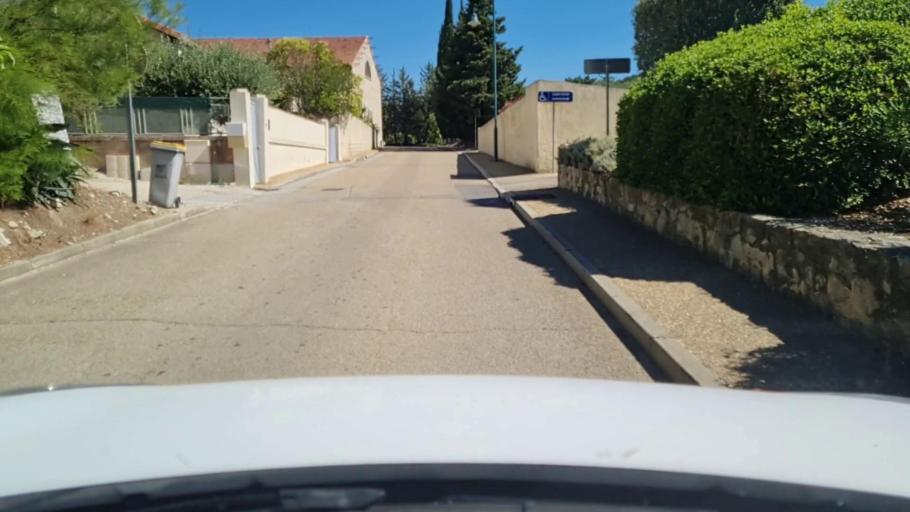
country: FR
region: Languedoc-Roussillon
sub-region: Departement du Gard
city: Villevieille
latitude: 43.8571
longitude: 4.1145
